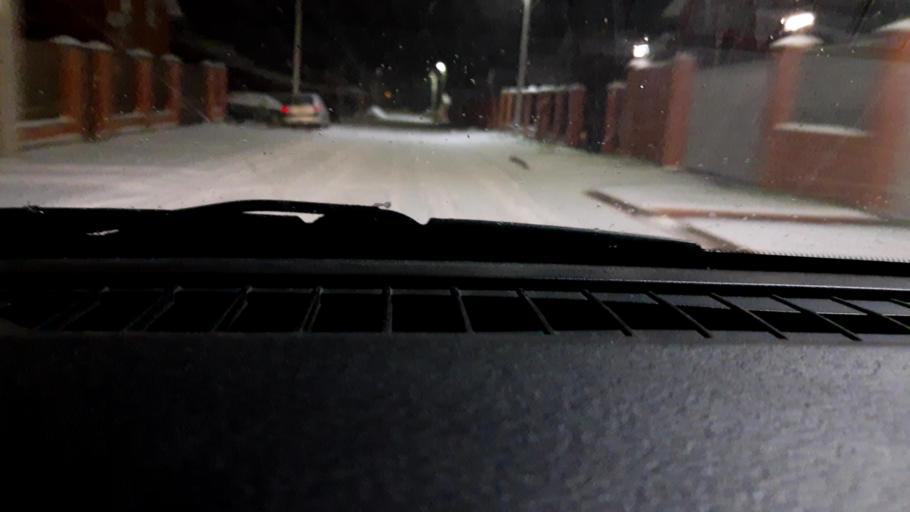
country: RU
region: Nizjnij Novgorod
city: Afonino
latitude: 56.2063
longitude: 44.1414
